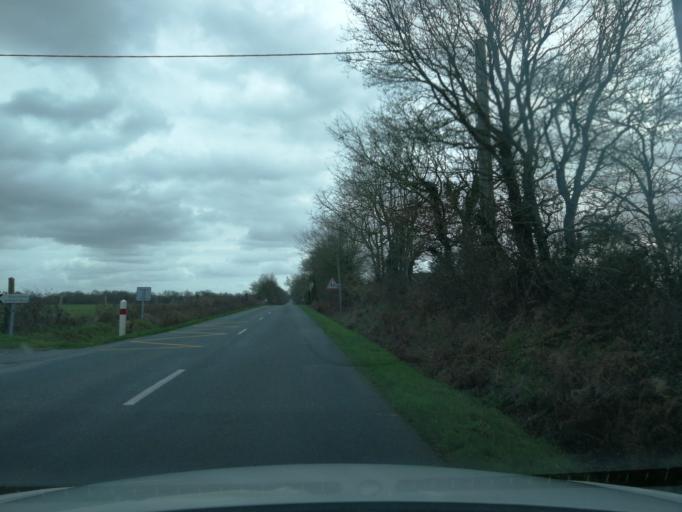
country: FR
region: Pays de la Loire
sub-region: Departement de la Loire-Atlantique
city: Montbert
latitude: 47.0234
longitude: -1.4920
